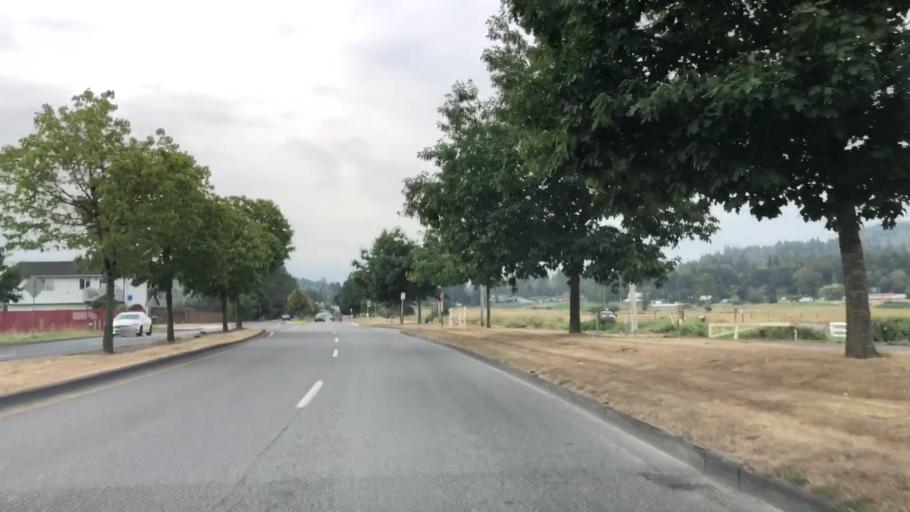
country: US
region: Washington
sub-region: Snohomish County
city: Monroe
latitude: 47.8566
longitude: -122.0120
